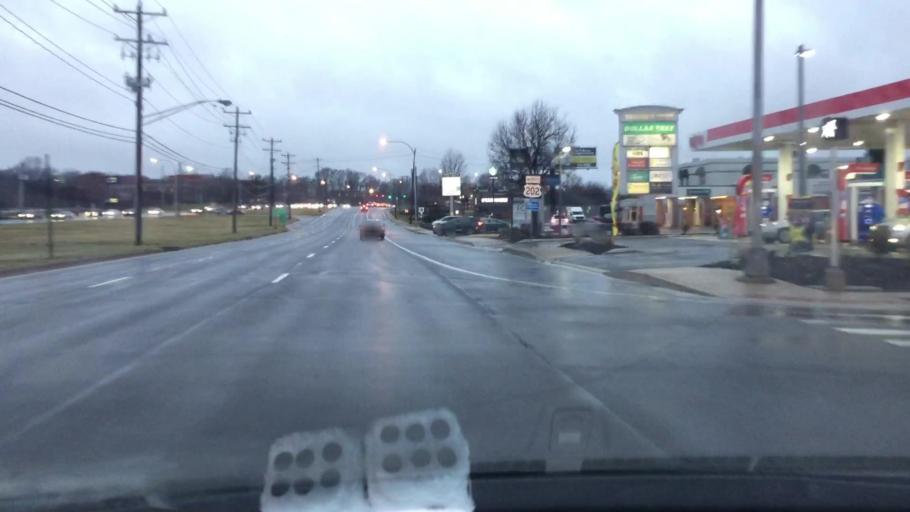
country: US
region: Delaware
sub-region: New Castle County
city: Greenville
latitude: 39.8075
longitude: -75.5489
